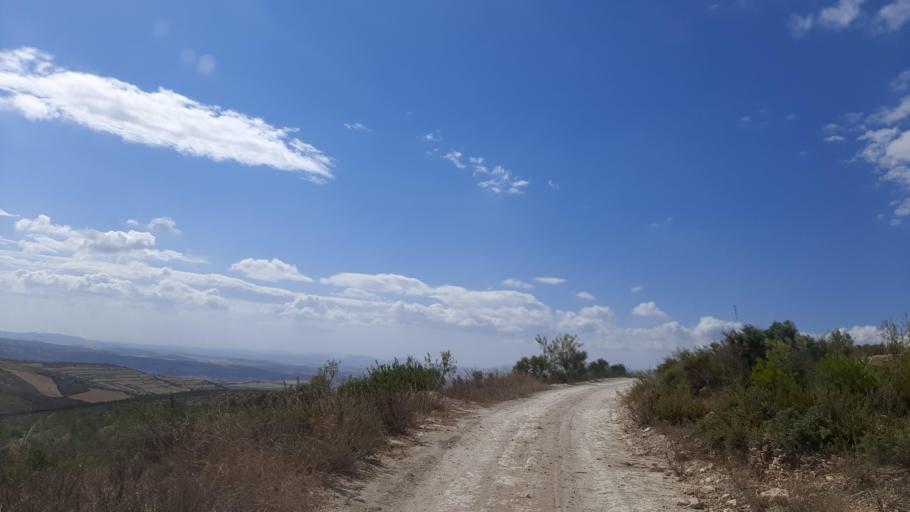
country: TN
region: Zaghwan
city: Zaghouan
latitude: 36.5045
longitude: 10.1844
